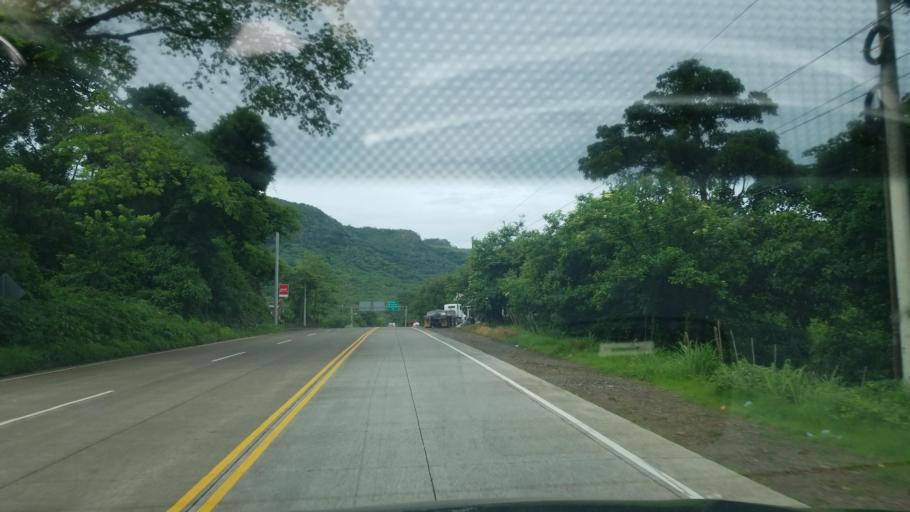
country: HN
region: Francisco Morazan
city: El Porvenir
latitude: 13.6935
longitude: -87.3289
